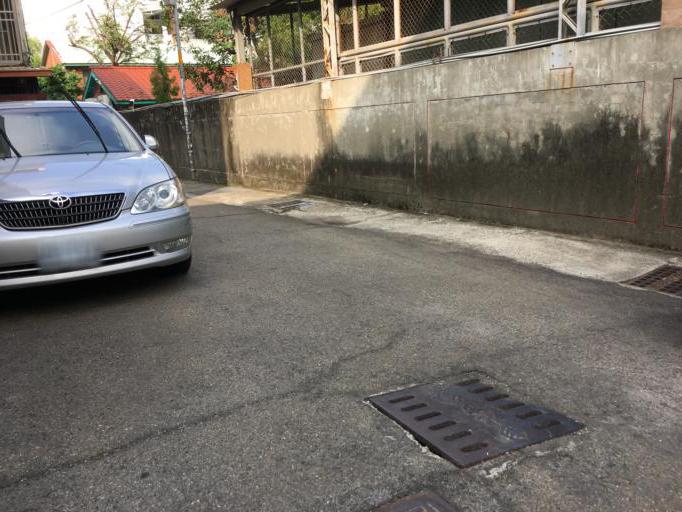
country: TW
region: Taiwan
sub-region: Changhua
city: Chang-hua
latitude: 24.0816
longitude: 120.5548
